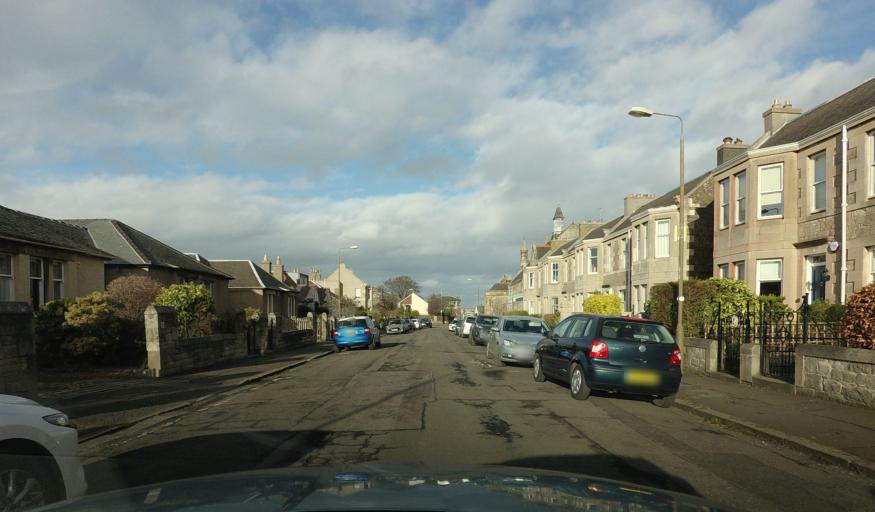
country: GB
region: Scotland
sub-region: Edinburgh
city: Edinburgh
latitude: 55.9782
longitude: -3.2114
